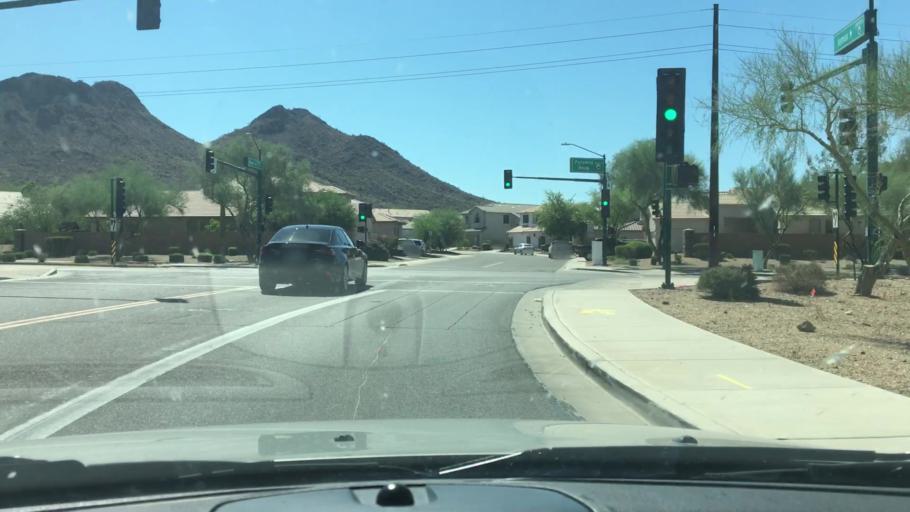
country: US
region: Arizona
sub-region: Maricopa County
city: Sun City
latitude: 33.7250
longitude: -112.2027
